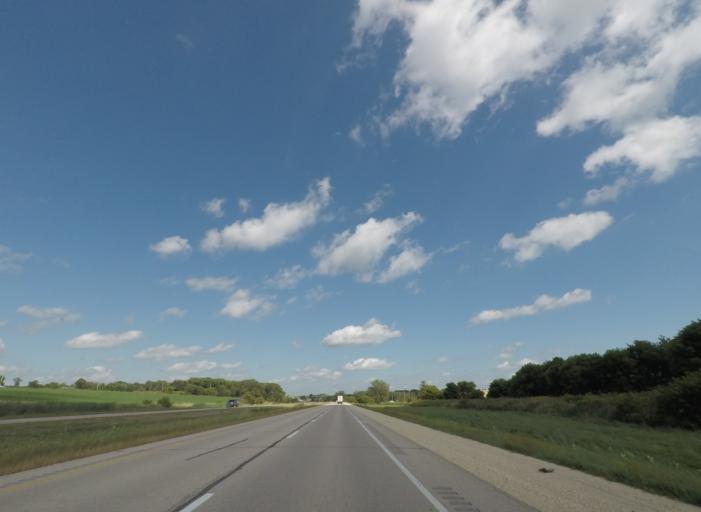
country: US
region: Iowa
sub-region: Dubuque County
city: Cascade
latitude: 42.3171
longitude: -90.9324
